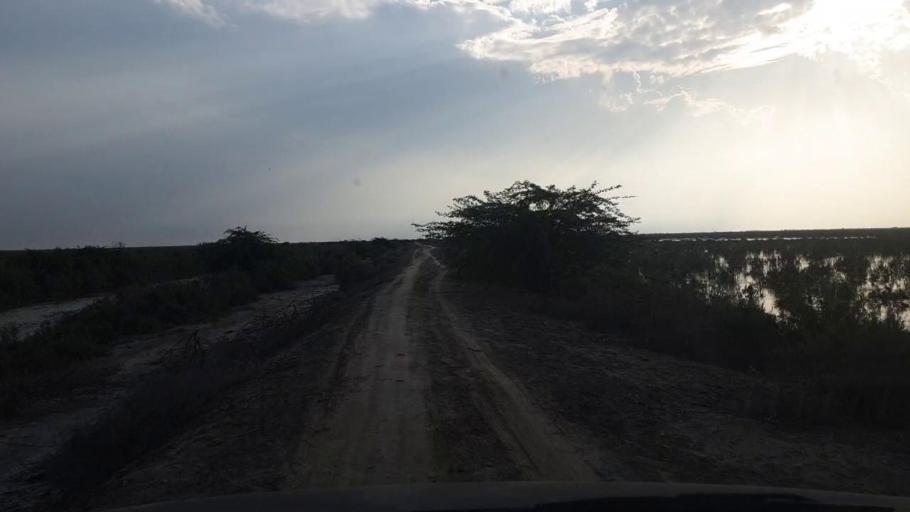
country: PK
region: Sindh
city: Badin
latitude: 24.4403
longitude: 68.6755
